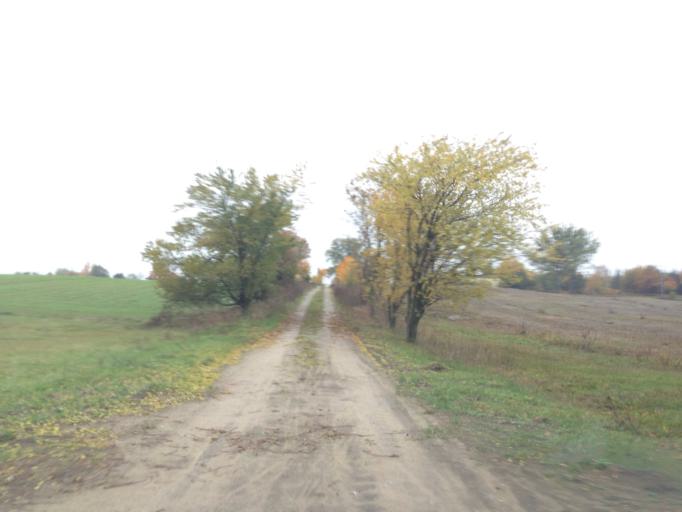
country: PL
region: Kujawsko-Pomorskie
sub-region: Powiat brodnicki
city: Gorzno
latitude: 53.2182
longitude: 19.6191
